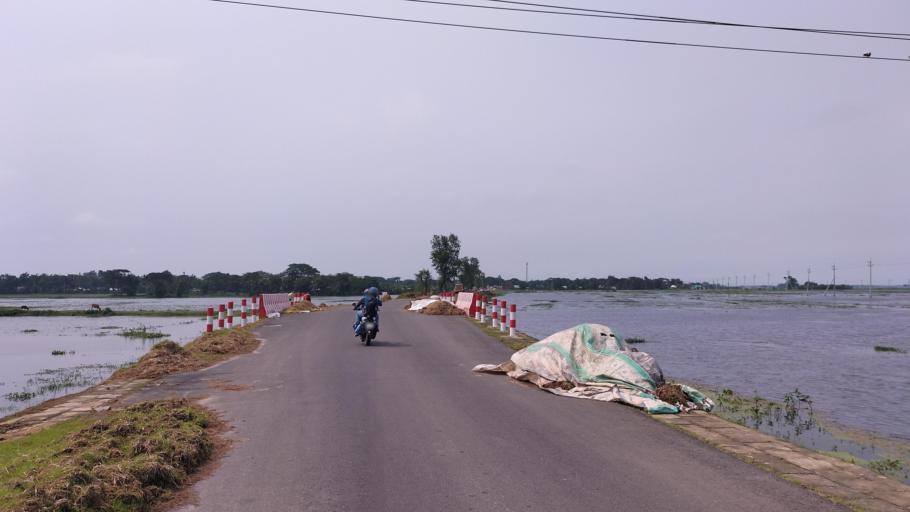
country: BD
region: Dhaka
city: Netrakona
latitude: 24.9612
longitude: 90.8337
